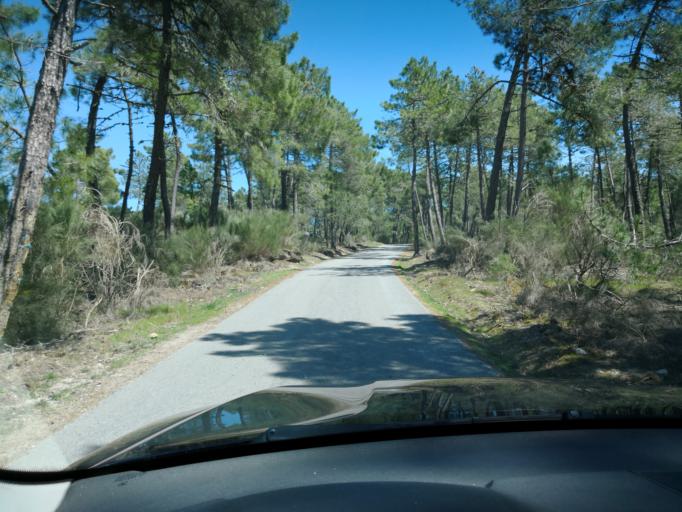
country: PT
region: Vila Real
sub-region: Vila Real
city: Vila Real
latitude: 41.3231
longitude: -7.6645
